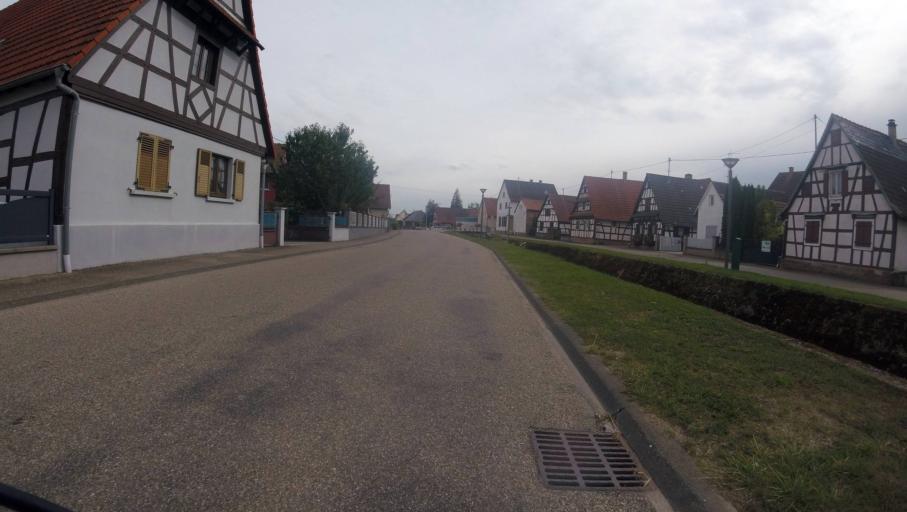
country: DE
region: Rheinland-Pfalz
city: Scheibenhardt
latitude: 48.9347
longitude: 8.1559
